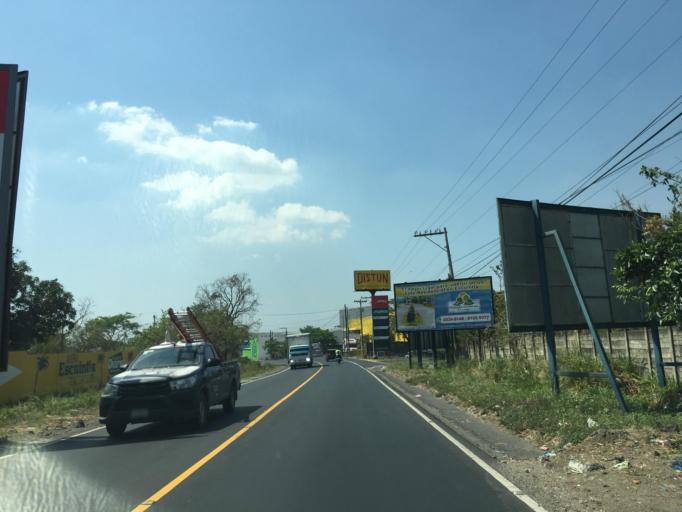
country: GT
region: Escuintla
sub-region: Municipio de Escuintla
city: Escuintla
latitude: 14.2959
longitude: -90.7959
